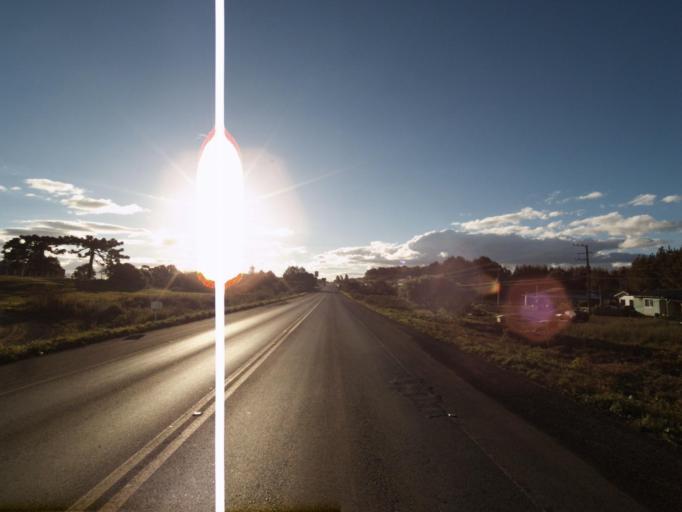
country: BR
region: Santa Catarina
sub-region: Campos Novos
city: Campos Novos
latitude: -27.3847
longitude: -51.2363
